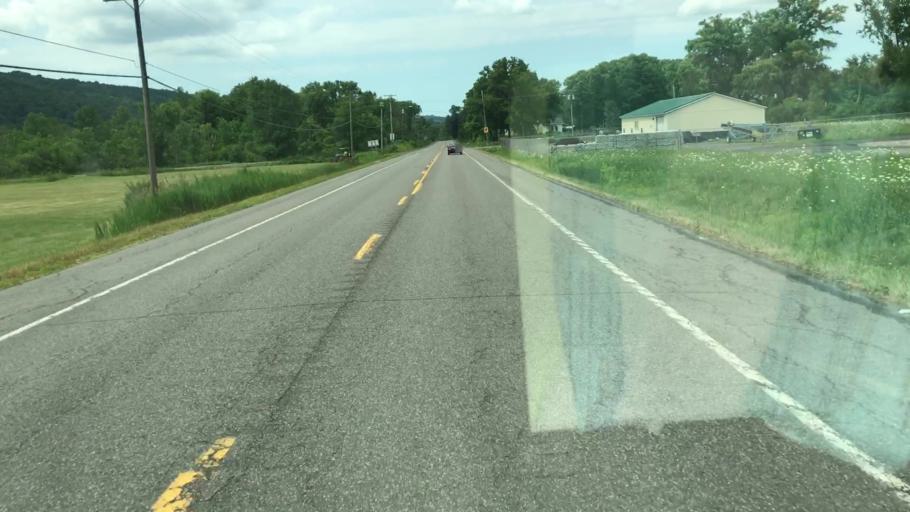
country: US
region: New York
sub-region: Onondaga County
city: Nedrow
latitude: 42.8950
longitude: -76.1548
